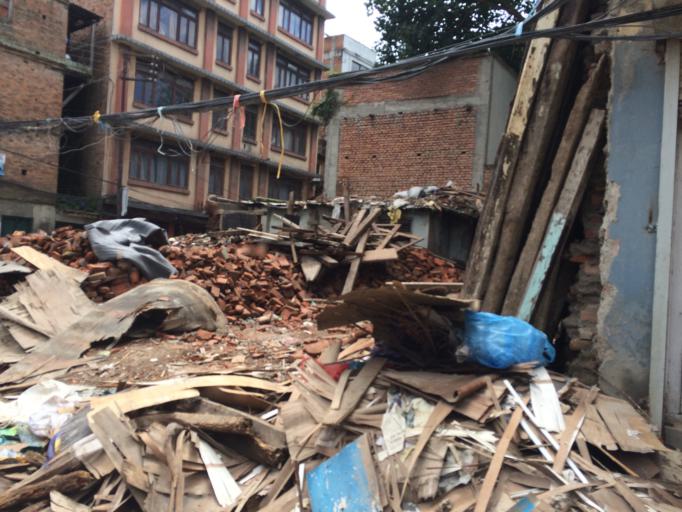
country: NP
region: Central Region
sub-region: Bagmati Zone
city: Kathmandu
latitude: 27.7057
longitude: 85.3067
